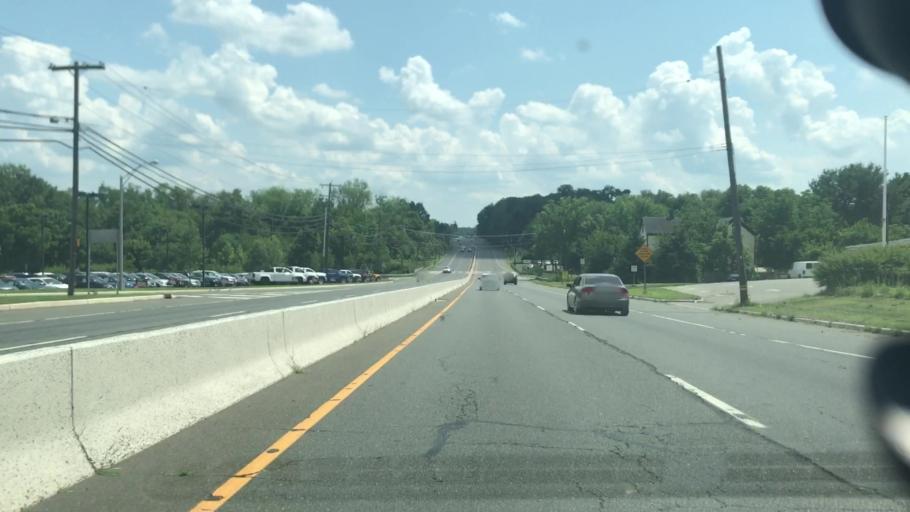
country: US
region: New Jersey
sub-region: Hunterdon County
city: Flemington
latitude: 40.4768
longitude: -74.8636
